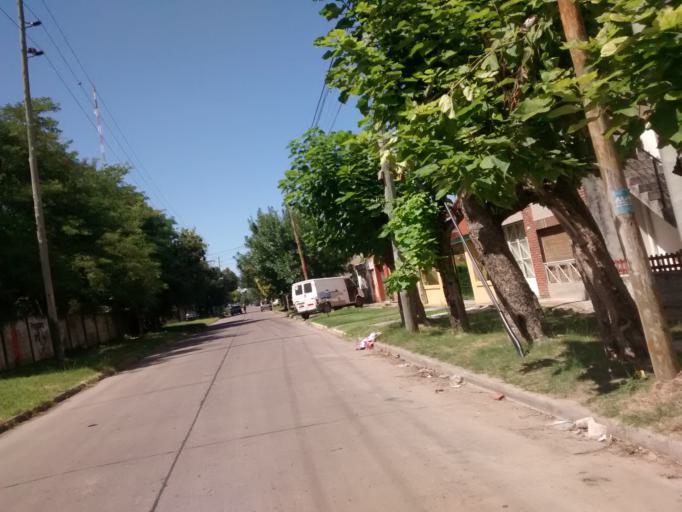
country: AR
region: Buenos Aires
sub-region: Partido de La Plata
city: La Plata
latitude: -34.9459
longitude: -57.9773
